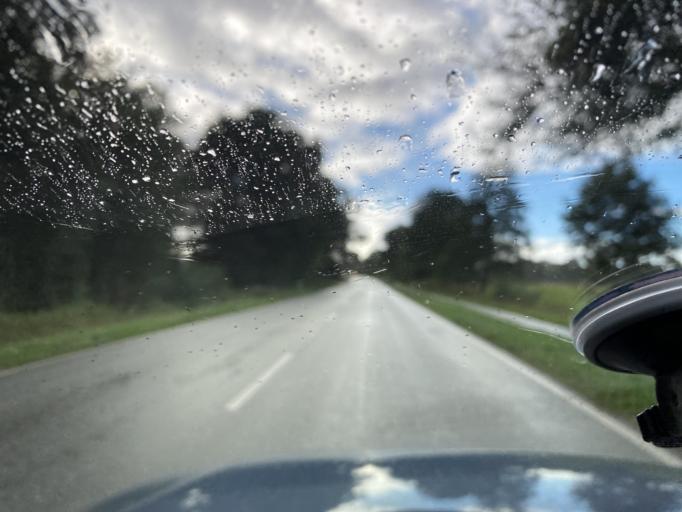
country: DE
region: Schleswig-Holstein
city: Tellingstedt
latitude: 54.2196
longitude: 9.3093
